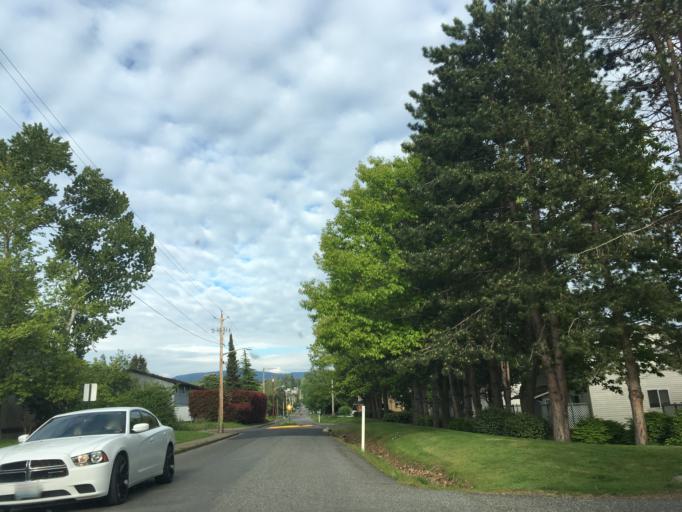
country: US
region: Washington
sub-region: Whatcom County
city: Bellingham
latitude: 48.7617
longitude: -122.4542
